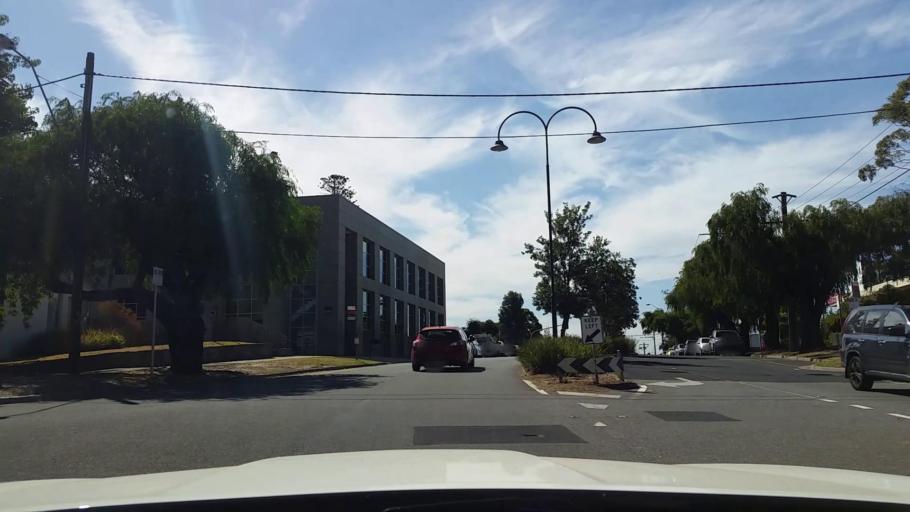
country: AU
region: Victoria
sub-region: Frankston
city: Frankston
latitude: -38.1474
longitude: 145.1217
